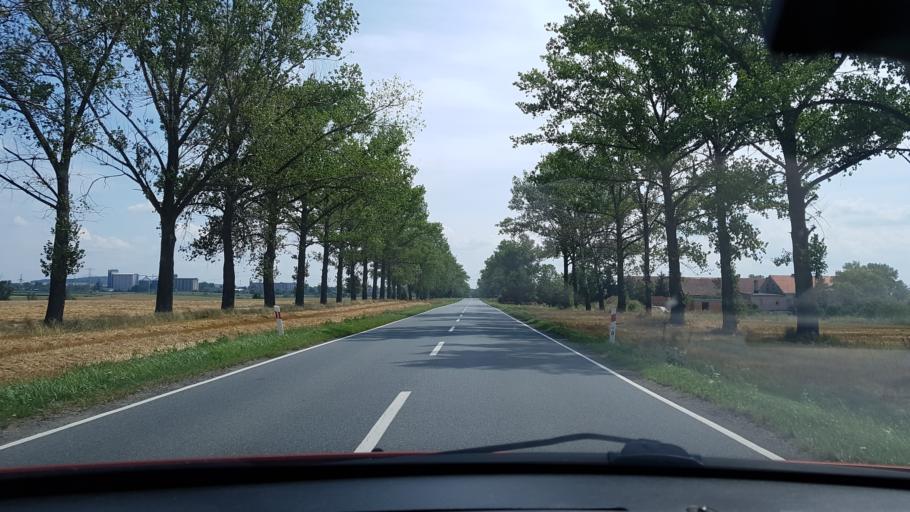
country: PL
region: Lower Silesian Voivodeship
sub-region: Powiat zabkowicki
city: Zabkowice Slaskie
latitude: 50.6067
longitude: 16.7891
